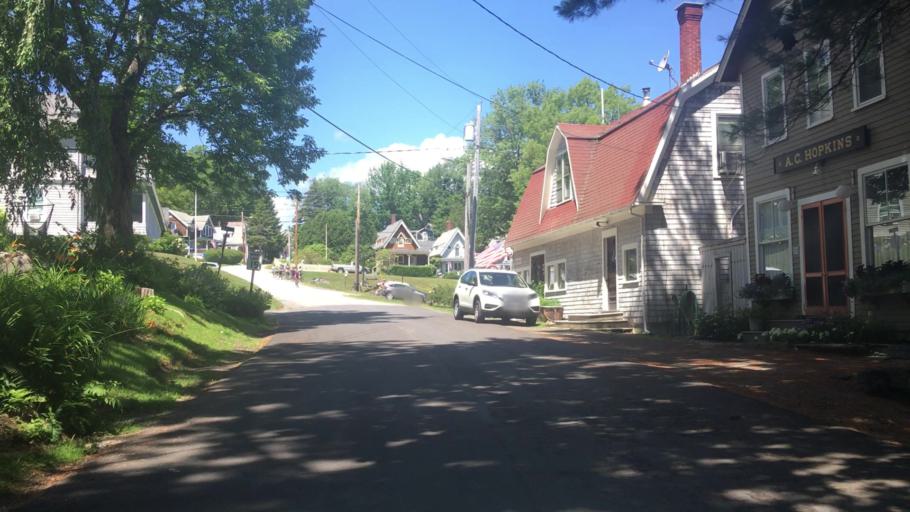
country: US
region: Maine
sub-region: Waldo County
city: Northport
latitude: 44.3799
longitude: -68.9676
